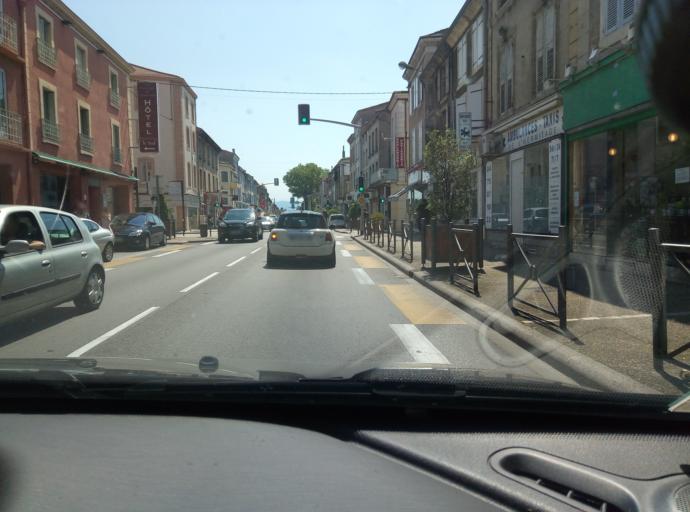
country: FR
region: Rhone-Alpes
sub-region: Departement de l'Ardeche
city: Tournon-sur-Rhone
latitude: 45.0701
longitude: 4.8385
